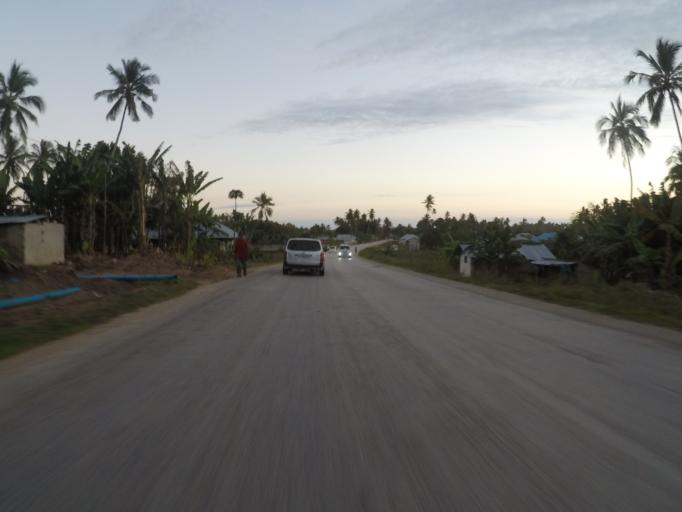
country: TZ
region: Zanzibar Central/South
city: Koani
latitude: -6.0285
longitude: 39.2381
